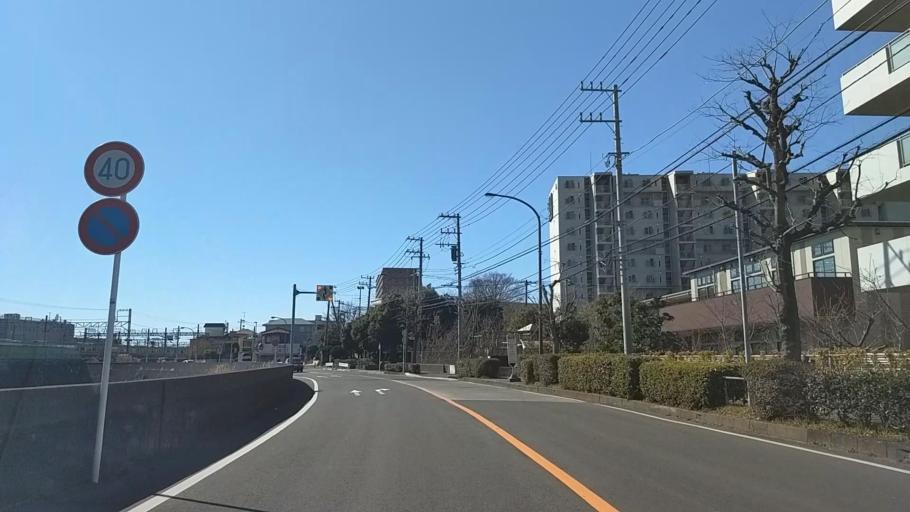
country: JP
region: Kanagawa
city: Kamakura
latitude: 35.3460
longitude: 139.5199
